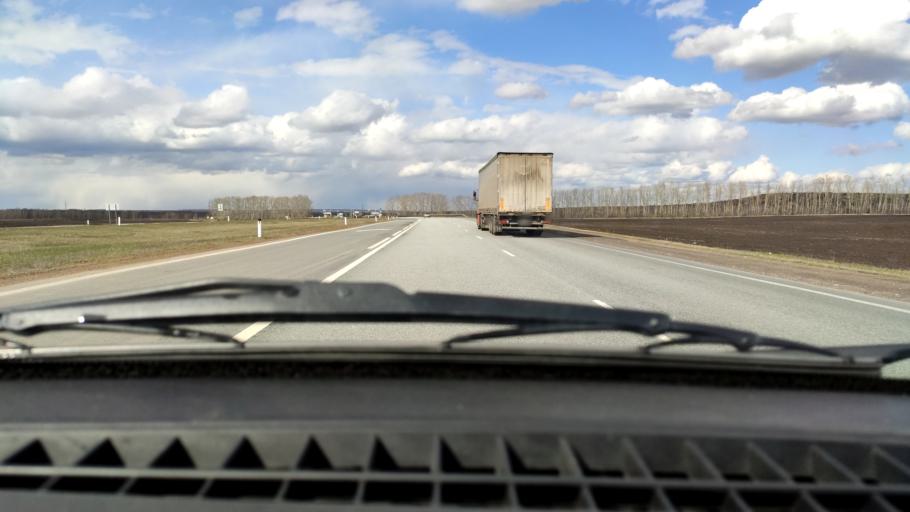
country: RU
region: Bashkortostan
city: Asanovo
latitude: 54.9530
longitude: 55.5848
